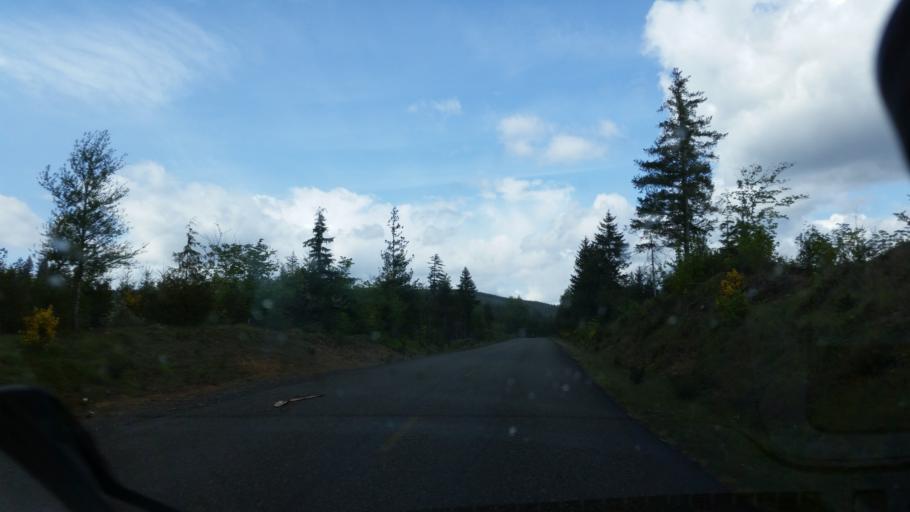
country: US
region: Washington
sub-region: Mason County
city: Shelton
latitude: 47.3277
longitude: -123.2798
